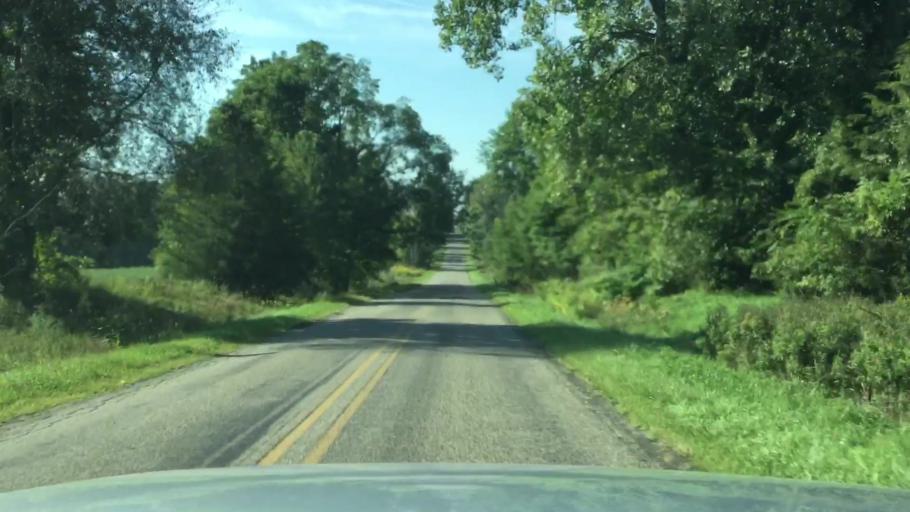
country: US
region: Michigan
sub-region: Lenawee County
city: Hudson
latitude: 41.8807
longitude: -84.4202
